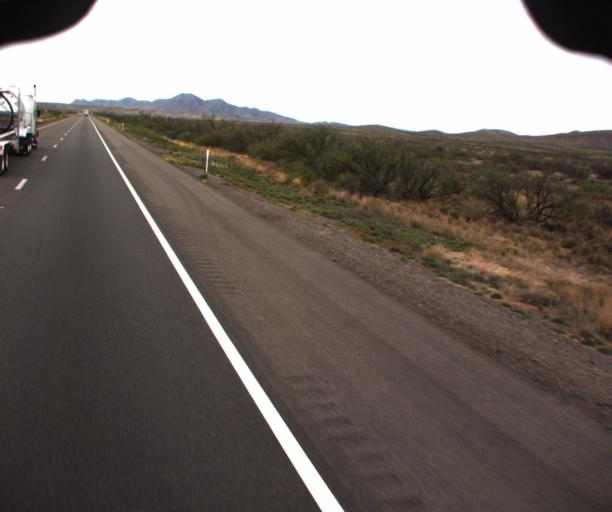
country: US
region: Arizona
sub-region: Cochise County
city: Willcox
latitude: 32.1619
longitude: -109.9742
